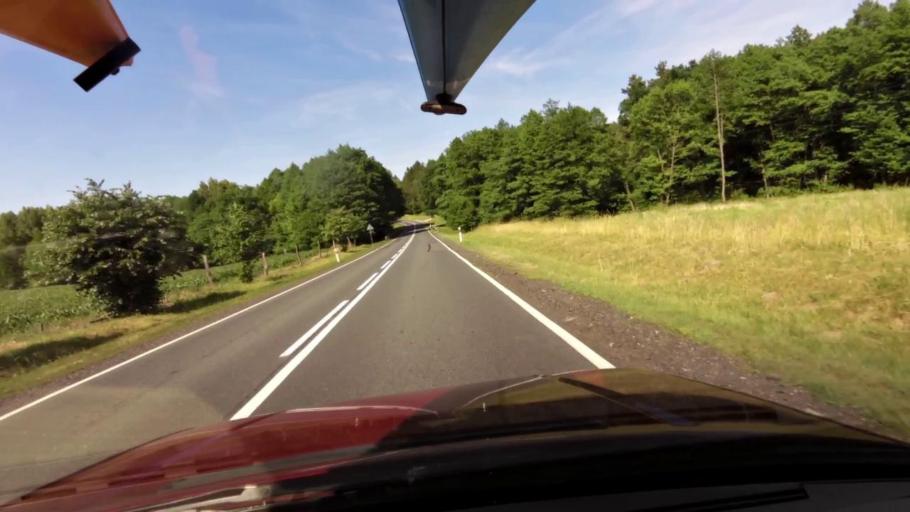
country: PL
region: Pomeranian Voivodeship
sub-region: Powiat bytowski
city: Miastko
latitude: 54.1127
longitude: 16.9971
